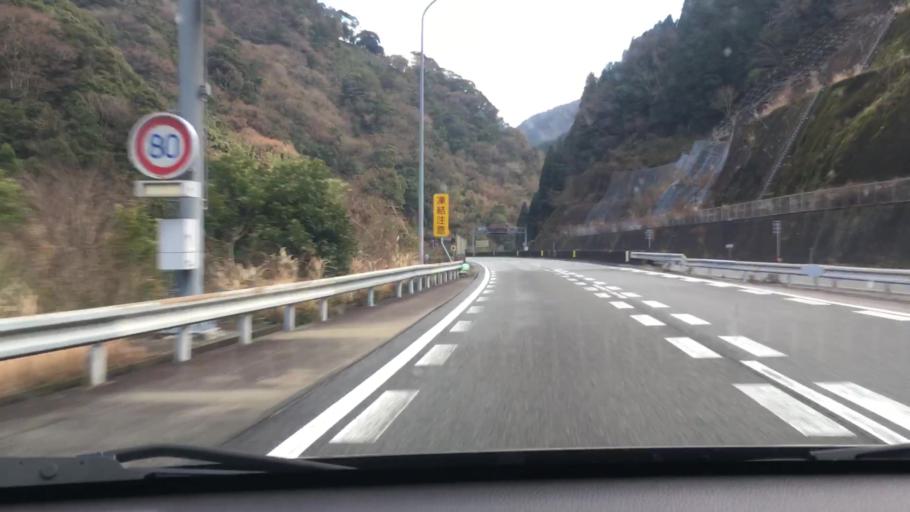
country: JP
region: Kumamoto
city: Hitoyoshi
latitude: 32.3388
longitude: 130.7315
